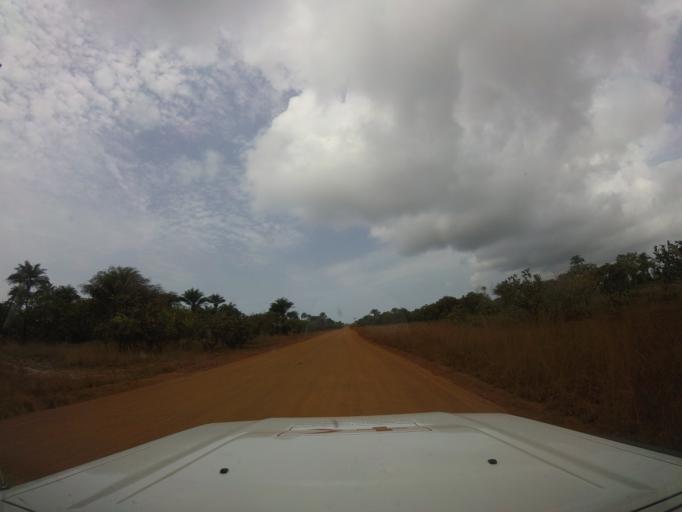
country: LR
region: Grand Cape Mount
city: Robertsport
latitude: 6.7058
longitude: -11.3005
